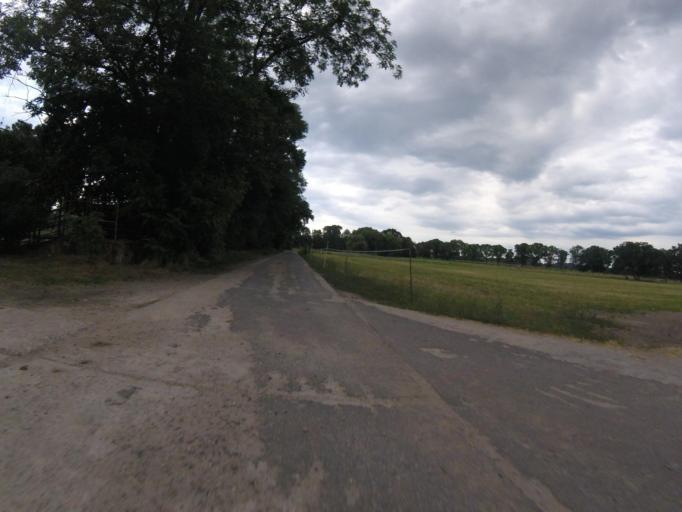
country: DE
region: Brandenburg
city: Mittenwalde
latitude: 52.2737
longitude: 13.5180
